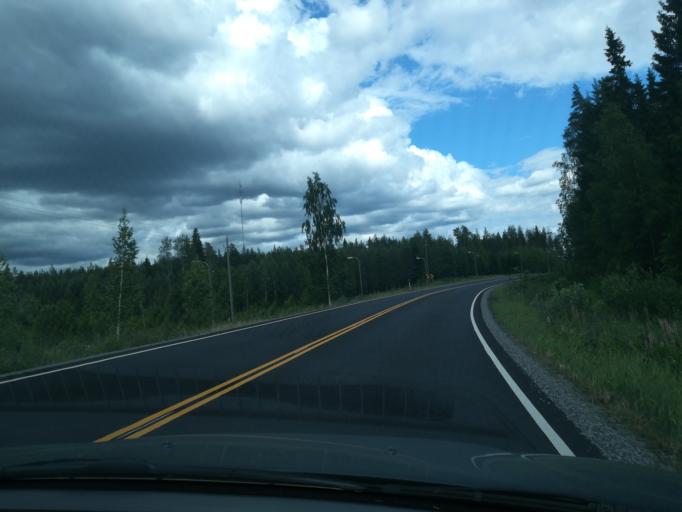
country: FI
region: Southern Savonia
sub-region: Mikkeli
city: Mikkeli
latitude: 61.6604
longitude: 27.1087
